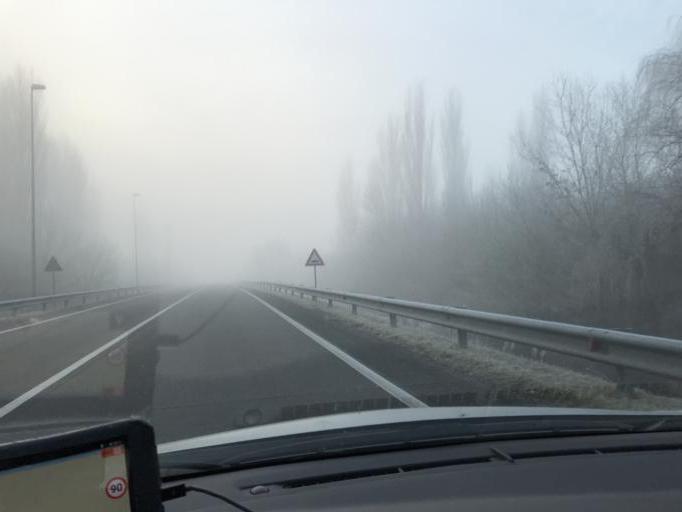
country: IT
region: Latium
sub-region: Provincia di Rieti
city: Limiti di Greccio
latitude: 42.4678
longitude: 12.7789
